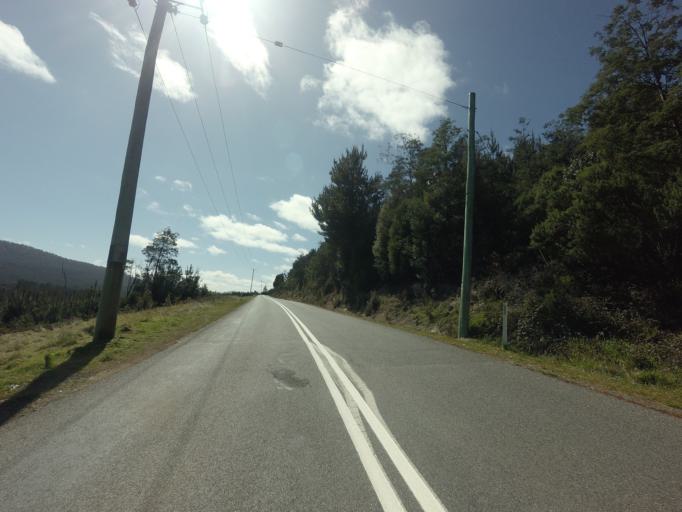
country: AU
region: Tasmania
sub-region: Derwent Valley
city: New Norfolk
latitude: -42.7455
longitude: 146.6535
